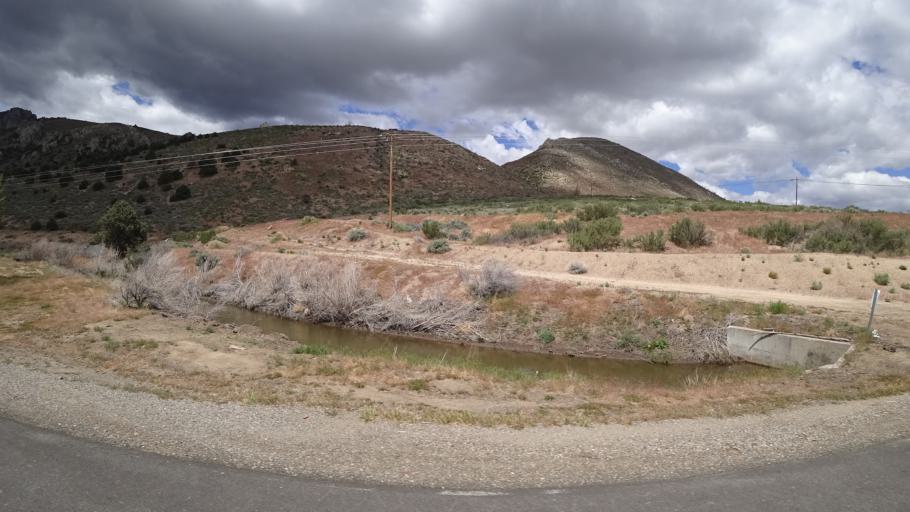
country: US
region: Nevada
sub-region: Lyon County
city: Smith Valley
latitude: 38.6305
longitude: -119.5239
